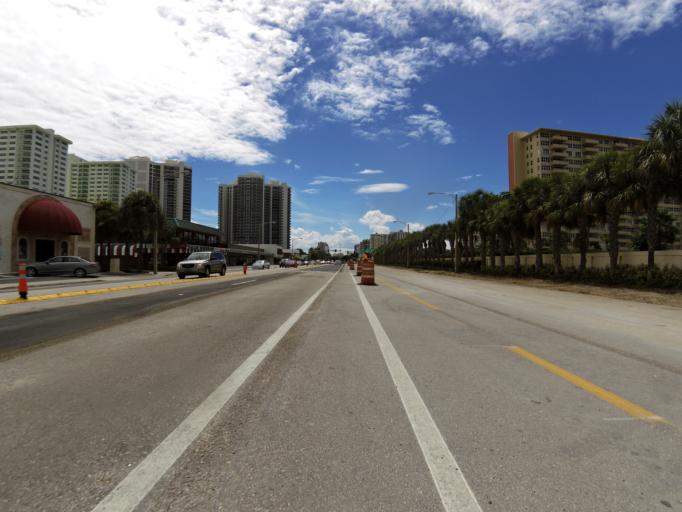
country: US
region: Florida
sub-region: Broward County
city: Lauderdale-by-the-Sea
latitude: 26.1716
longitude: -80.0999
